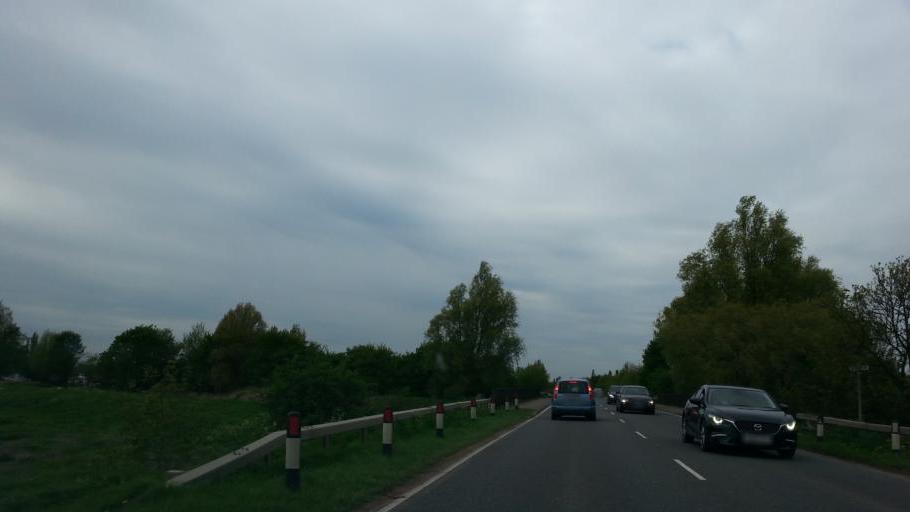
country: GB
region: England
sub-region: Cambridgeshire
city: March
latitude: 52.5527
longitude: 0.0681
